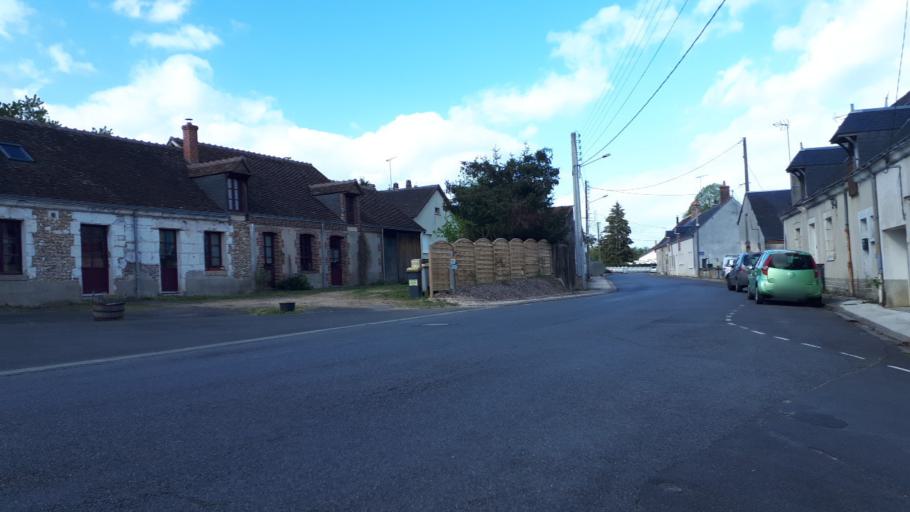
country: FR
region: Centre
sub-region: Departement du Loir-et-Cher
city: Aze
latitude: 47.8515
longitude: 0.9985
